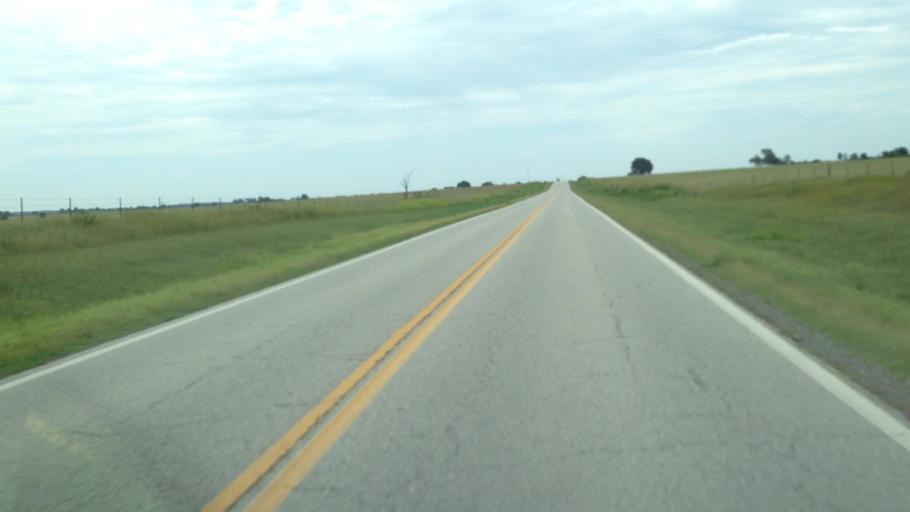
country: US
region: Kansas
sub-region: Labette County
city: Chetopa
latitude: 36.8499
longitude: -95.1215
